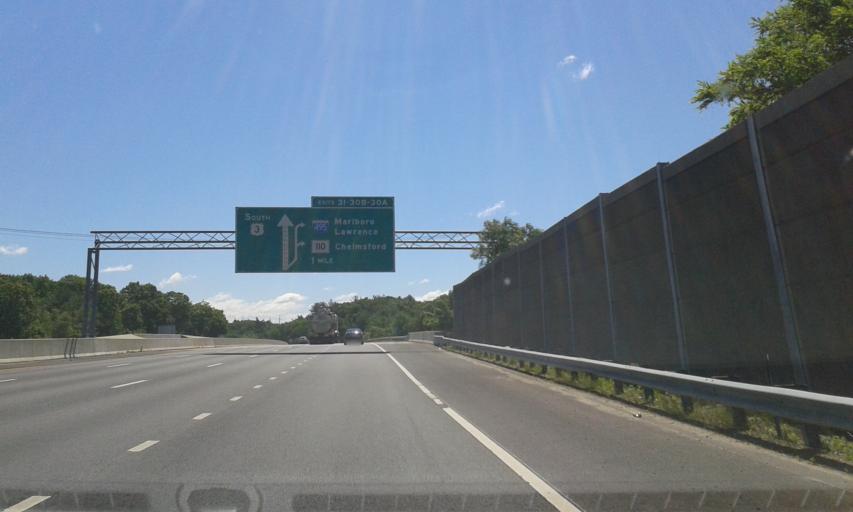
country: US
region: Massachusetts
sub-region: Middlesex County
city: Chelmsford
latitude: 42.6210
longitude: -71.3608
